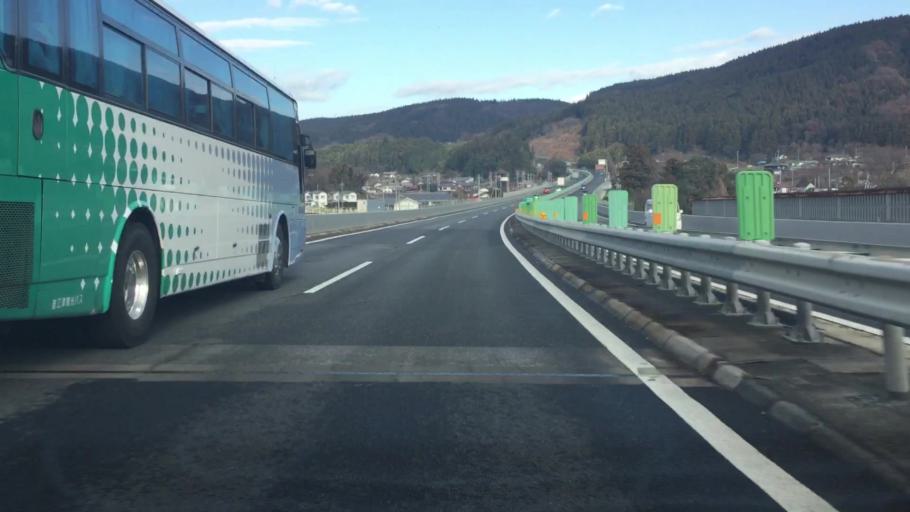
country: JP
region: Gunma
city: Annaka
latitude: 36.3163
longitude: 138.7732
